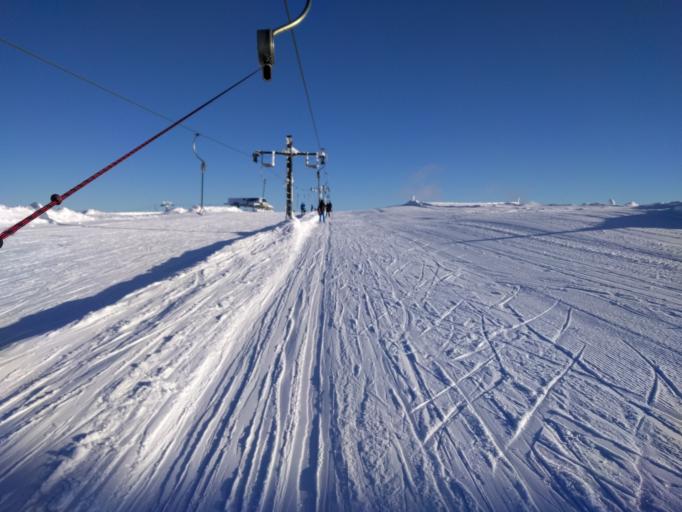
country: NO
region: Hedmark
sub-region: Trysil
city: Innbygda
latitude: 61.1746
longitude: 13.0197
